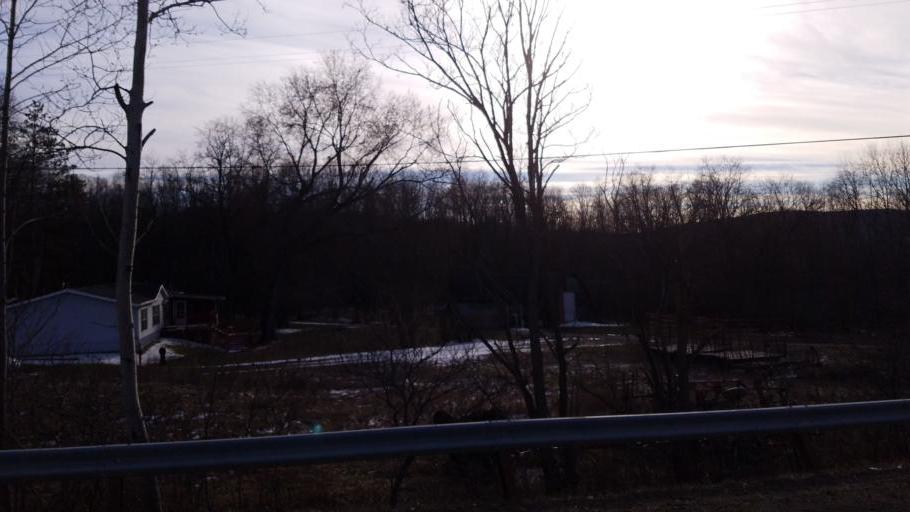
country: US
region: New York
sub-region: Allegany County
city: Wellsville
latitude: 42.1696
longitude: -77.9681
